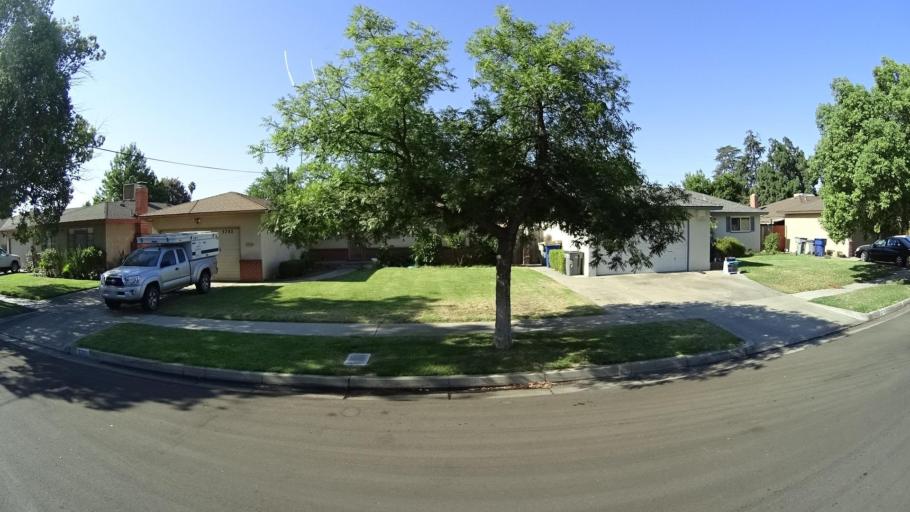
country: US
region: California
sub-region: Fresno County
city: Fresno
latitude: 36.7909
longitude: -119.7615
